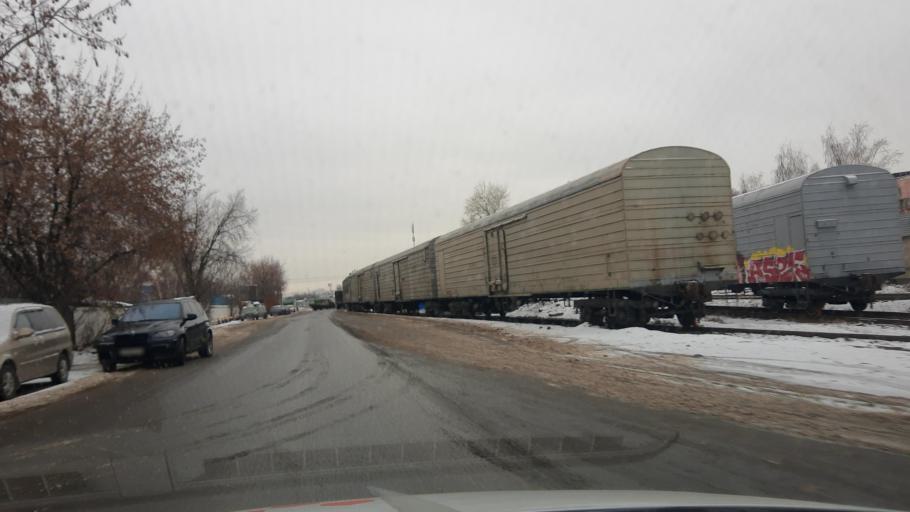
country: RU
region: Moscow
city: Lyublino
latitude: 55.6758
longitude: 37.7359
